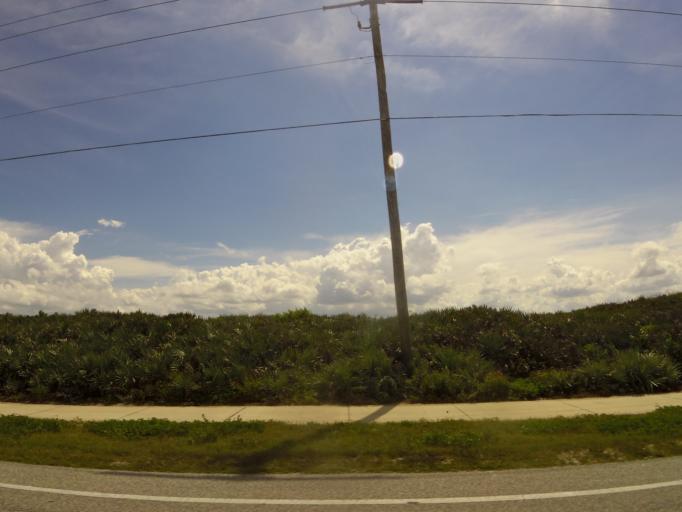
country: US
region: Florida
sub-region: Flagler County
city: Flagler Beach
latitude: 29.4227
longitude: -81.1005
